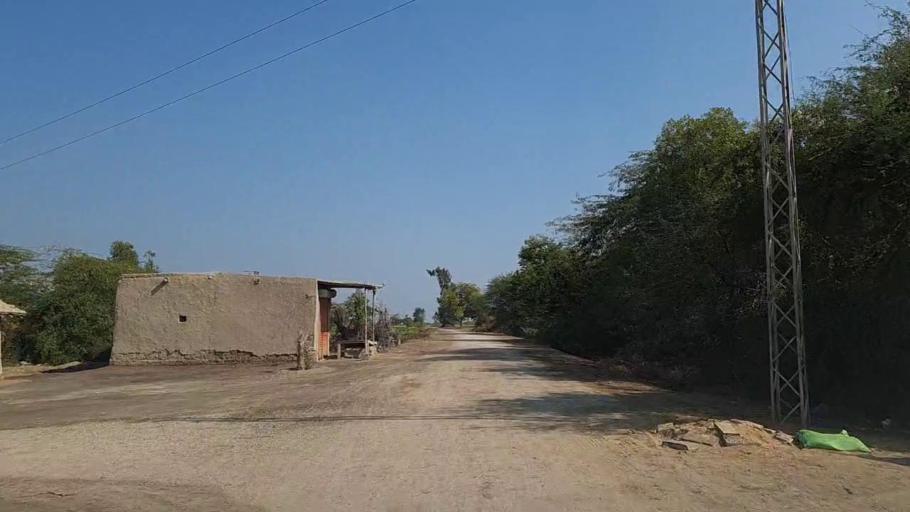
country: PK
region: Sindh
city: Jam Sahib
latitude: 26.2551
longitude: 68.5785
